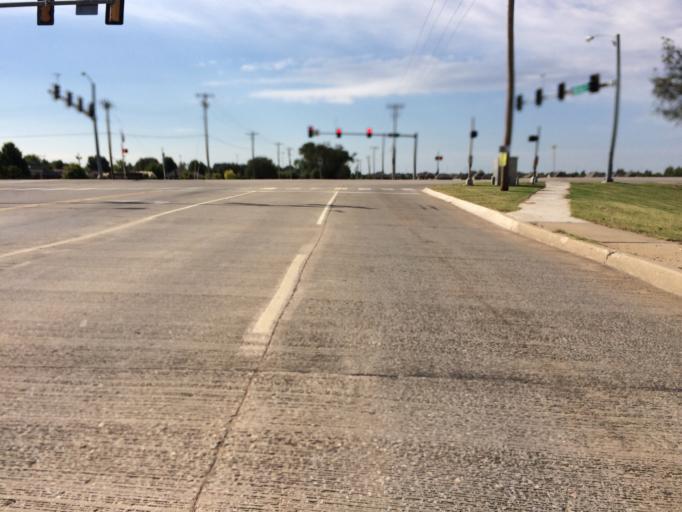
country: US
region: Oklahoma
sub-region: Cleveland County
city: Norman
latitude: 35.1891
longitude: -97.4059
